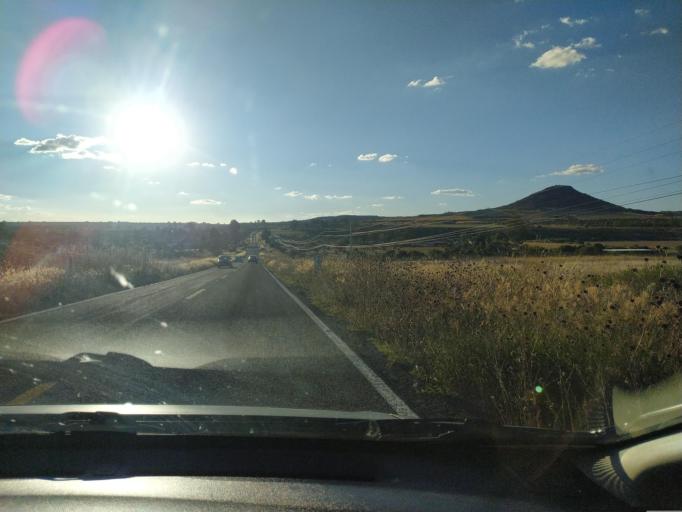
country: MX
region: Jalisco
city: San Diego de Alejandria
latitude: 21.0033
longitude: -102.0866
